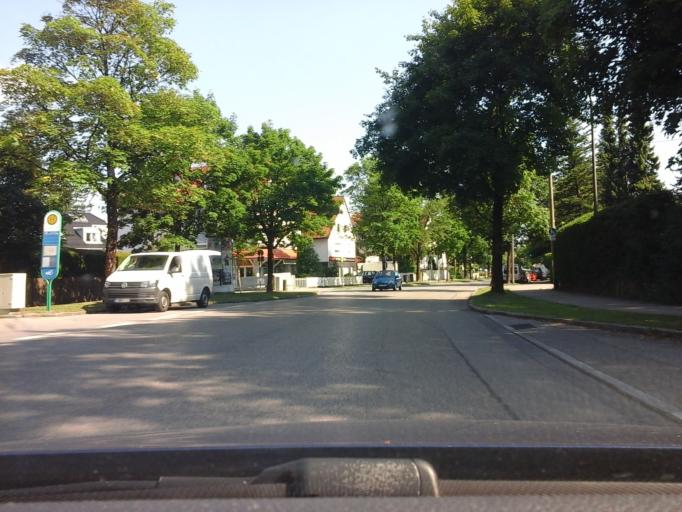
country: DE
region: Bavaria
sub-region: Upper Bavaria
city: Unterhaching
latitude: 48.0757
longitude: 11.6034
